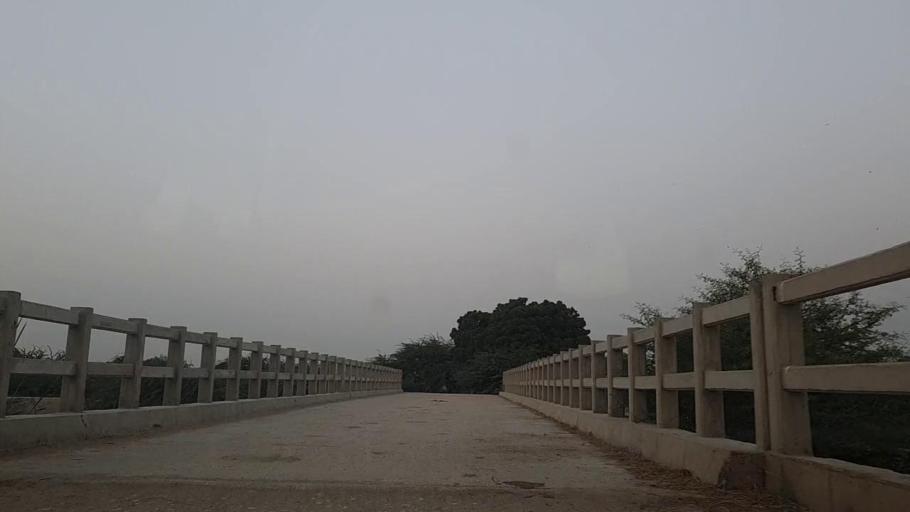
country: PK
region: Sindh
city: Mirpur Sakro
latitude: 24.5741
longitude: 67.7884
